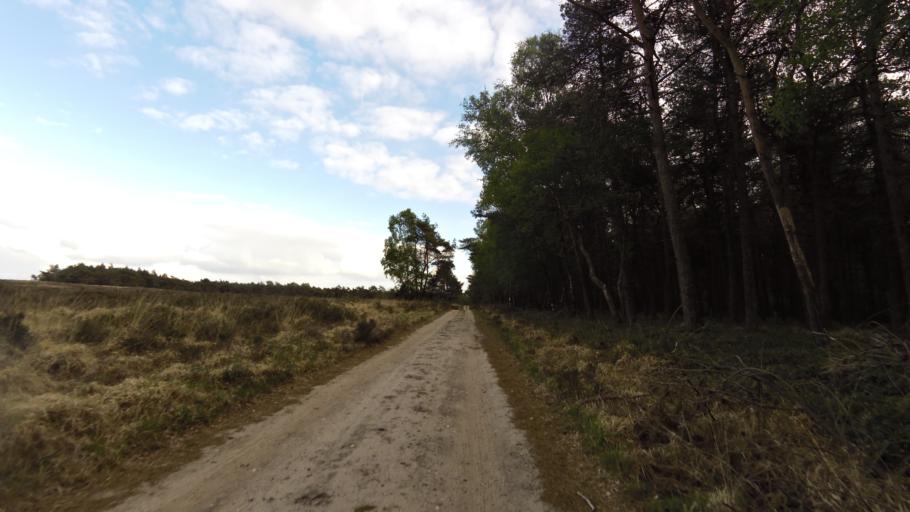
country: NL
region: Gelderland
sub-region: Gemeente Rozendaal
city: Rozendaal
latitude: 52.0434
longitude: 5.9556
